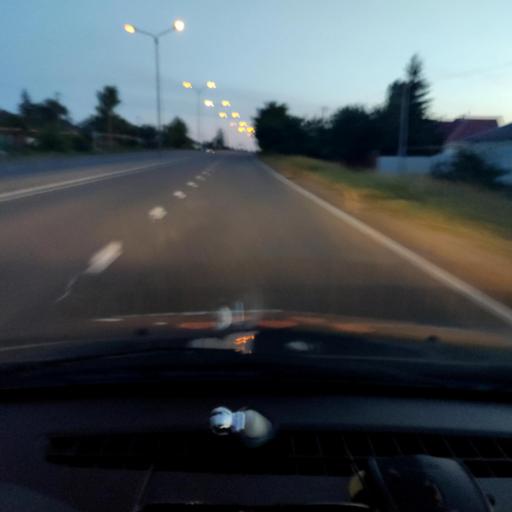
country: RU
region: Belgorod
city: Gubkin
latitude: 51.2742
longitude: 37.5868
